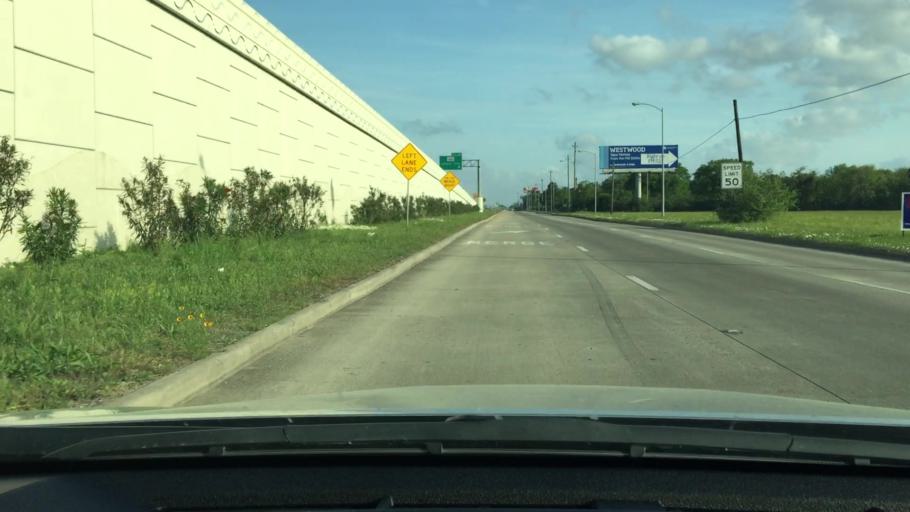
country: US
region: Texas
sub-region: Harris County
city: Webster
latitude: 29.5205
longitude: -95.1249
